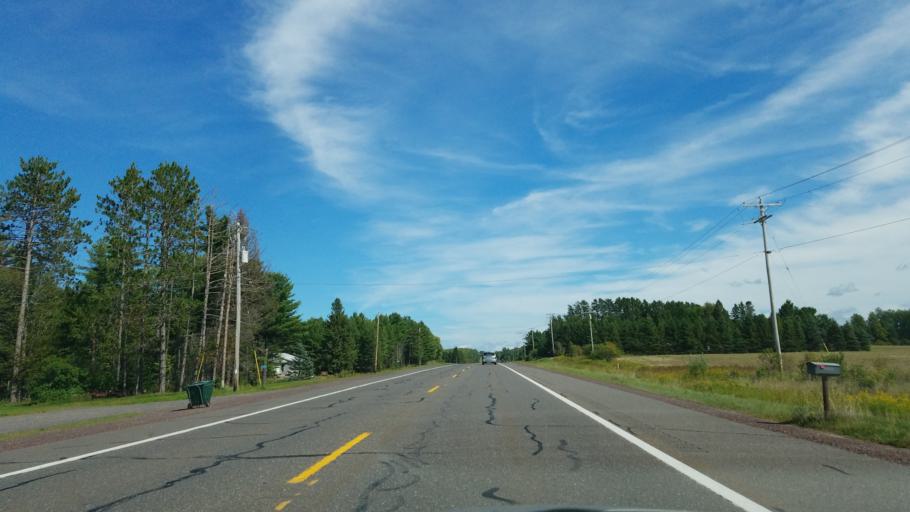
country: US
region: Michigan
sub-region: Ontonagon County
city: Ontonagon
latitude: 46.5348
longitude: -89.1624
